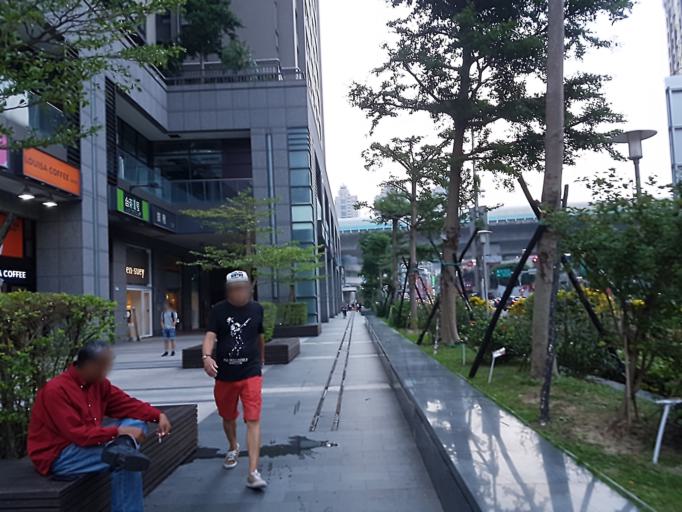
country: TW
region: Taipei
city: Taipei
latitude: 24.9571
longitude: 121.5381
